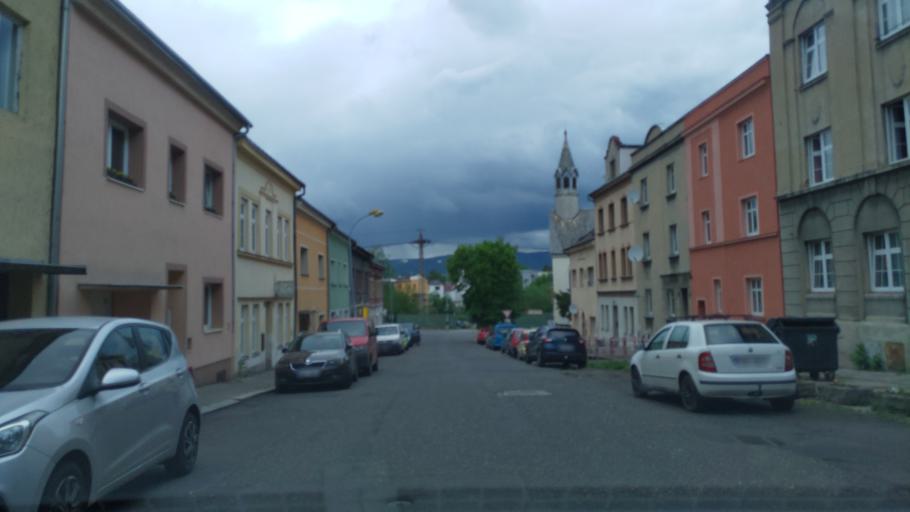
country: CZ
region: Ustecky
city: Trmice
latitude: 50.6415
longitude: 14.0026
